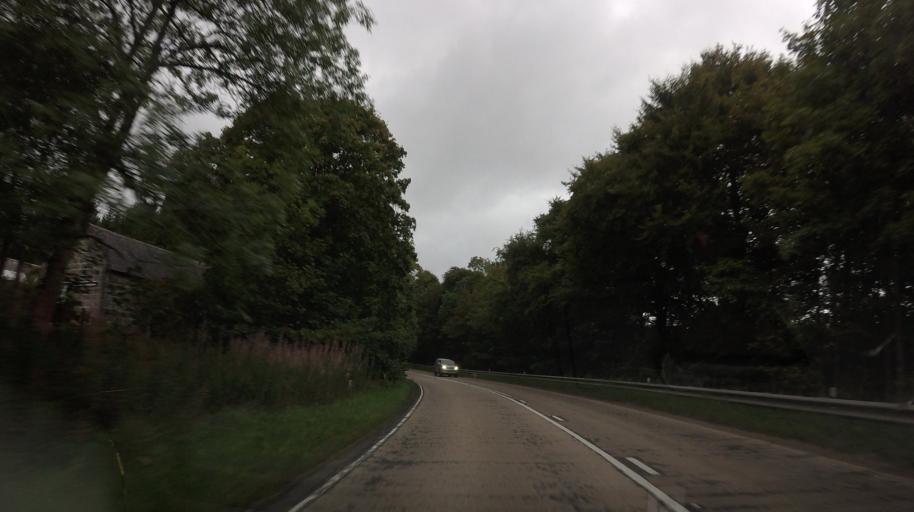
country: GB
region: Scotland
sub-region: Aberdeenshire
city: Torphins
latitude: 57.1940
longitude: -2.5774
